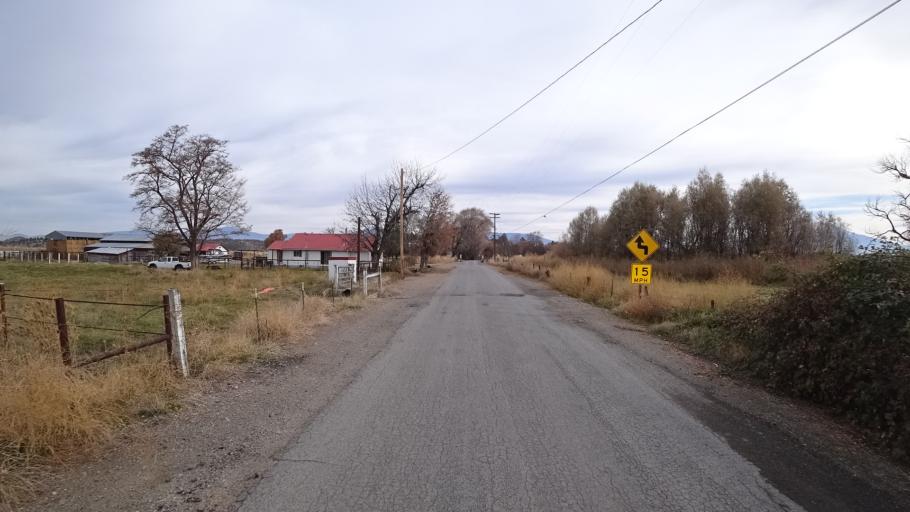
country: US
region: California
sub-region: Siskiyou County
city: Montague
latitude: 41.6582
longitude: -122.5120
